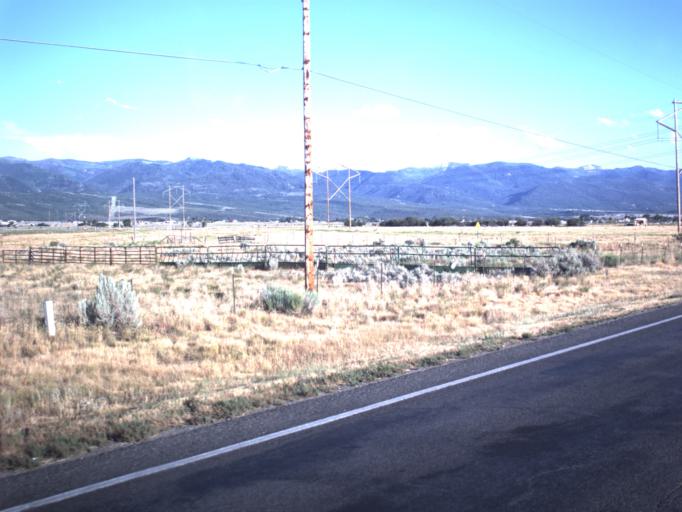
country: US
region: Utah
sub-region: Sanpete County
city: Mount Pleasant
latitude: 39.5688
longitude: -111.4555
